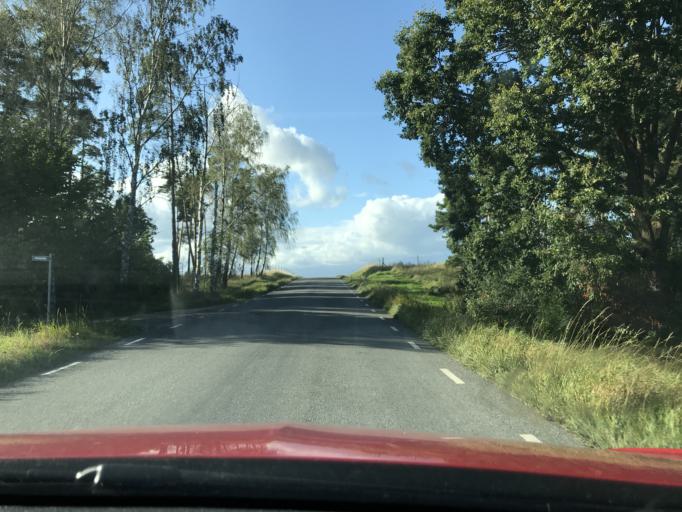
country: SE
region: Skane
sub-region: Kristianstads Kommun
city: Degeberga
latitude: 55.8512
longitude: 14.0790
